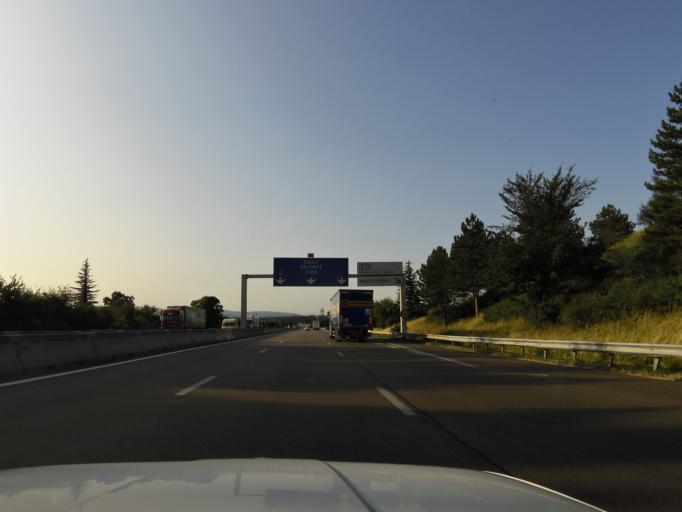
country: FR
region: Rhone-Alpes
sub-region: Departement de l'Ardeche
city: Cruas
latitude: 44.6655
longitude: 4.7969
